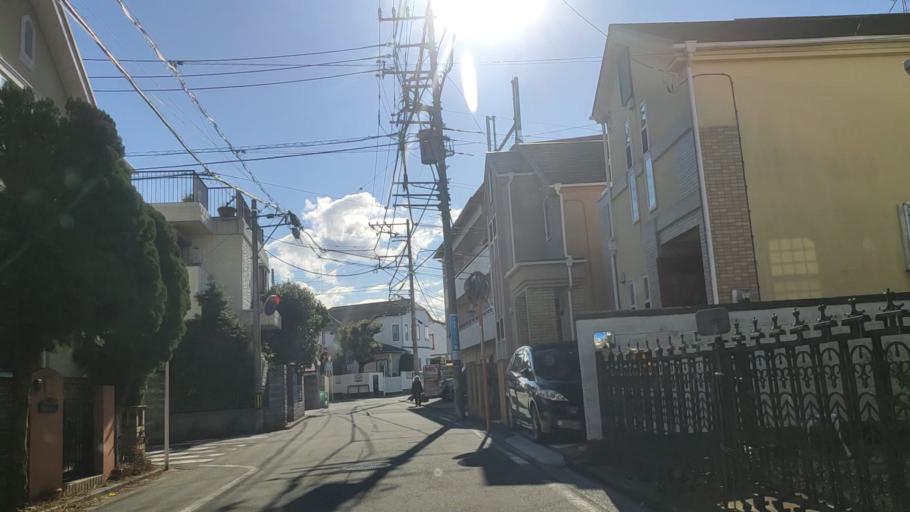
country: JP
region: Kanagawa
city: Yokohama
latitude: 35.4256
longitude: 139.6489
